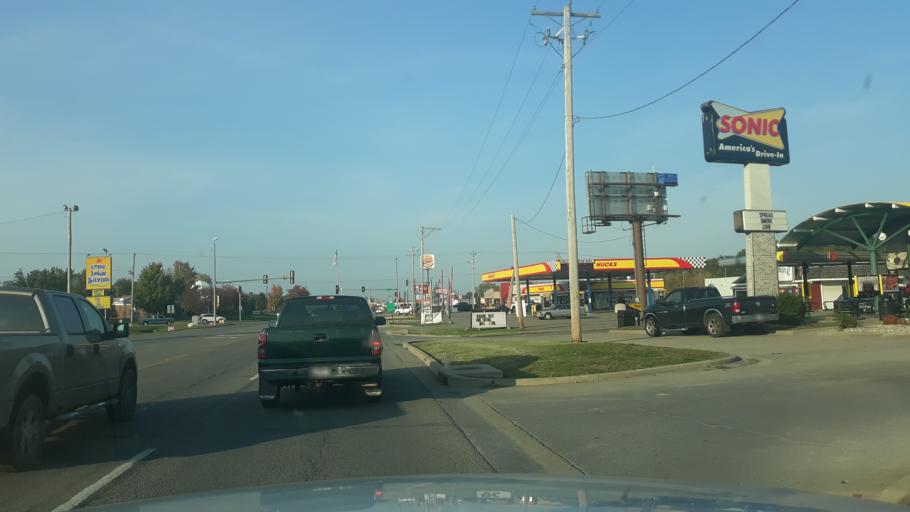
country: US
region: Illinois
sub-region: Saline County
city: Harrisburg
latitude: 37.7298
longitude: -88.5359
